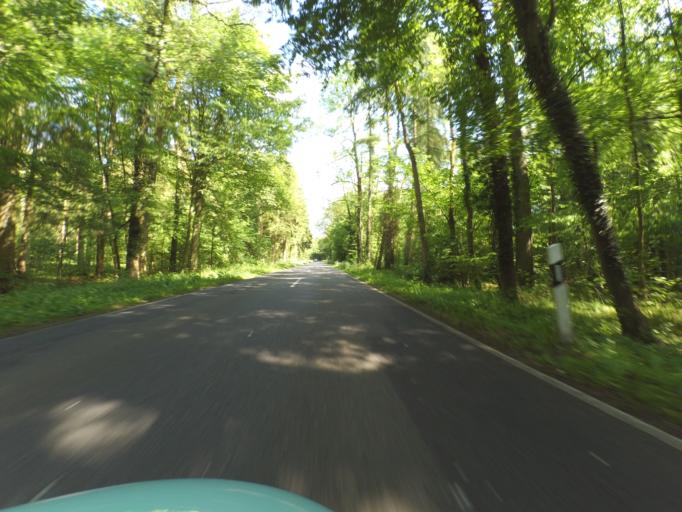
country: DE
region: Lower Saxony
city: Nienhagen
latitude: 52.5332
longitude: 10.0946
